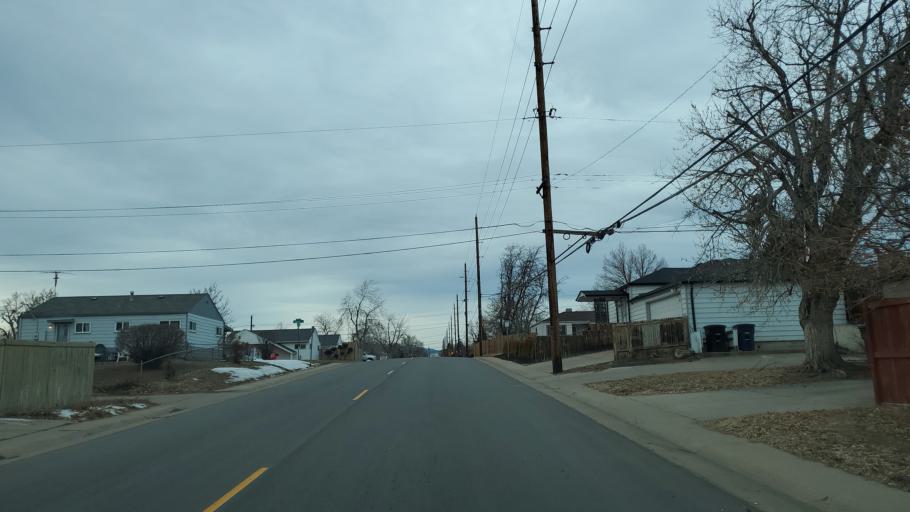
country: US
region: Colorado
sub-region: Arapahoe County
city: Englewood
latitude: 39.6931
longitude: -105.0069
